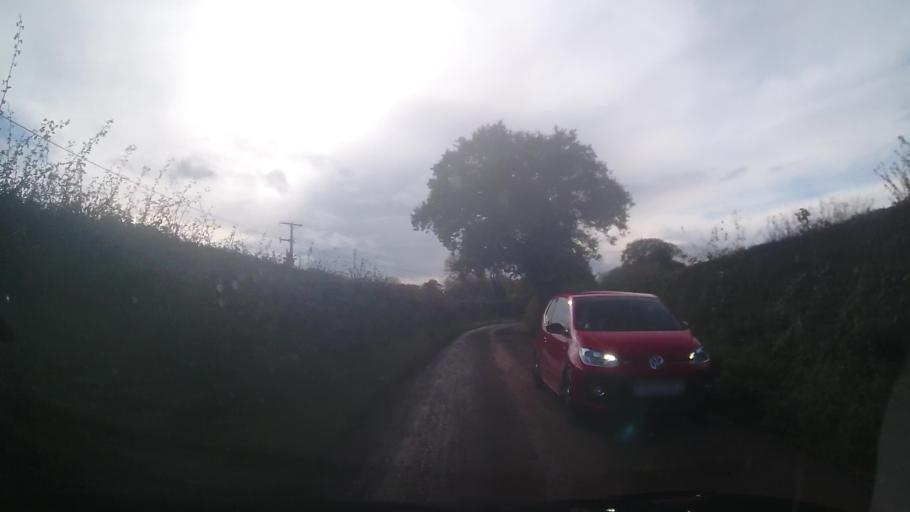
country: GB
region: England
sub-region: Shropshire
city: Whitchurch
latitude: 52.9456
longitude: -2.7011
